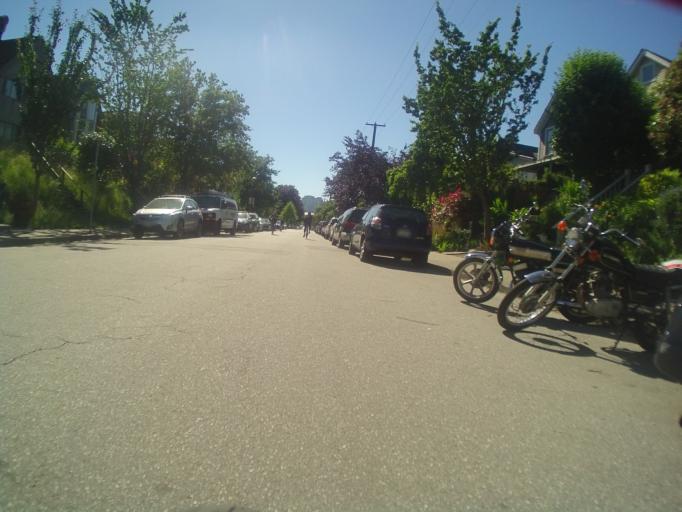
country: CA
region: British Columbia
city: Vancouver
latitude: 49.2775
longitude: -123.0900
